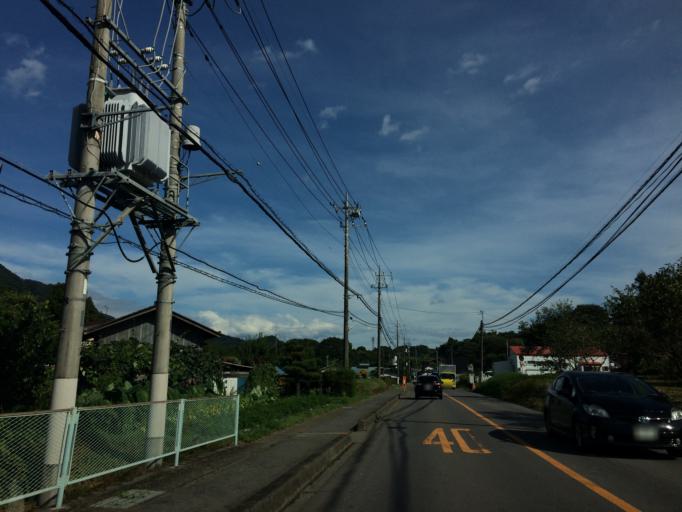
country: JP
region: Gunma
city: Nakanojomachi
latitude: 36.5672
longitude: 138.8756
